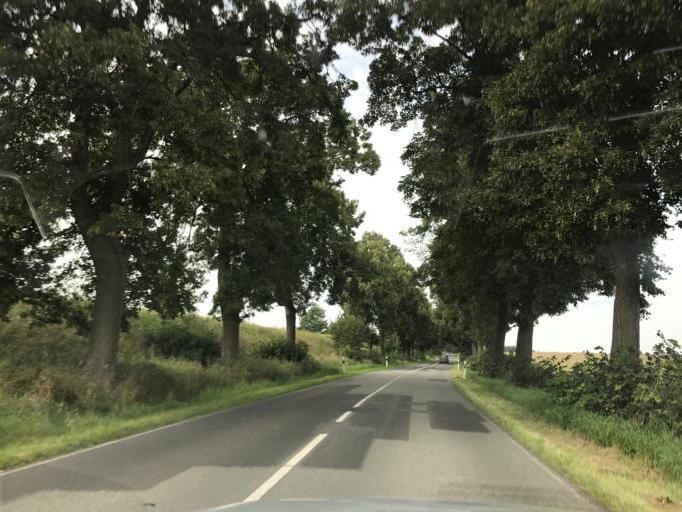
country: DE
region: Mecklenburg-Vorpommern
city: Rechlin
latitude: 53.3210
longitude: 12.7244
